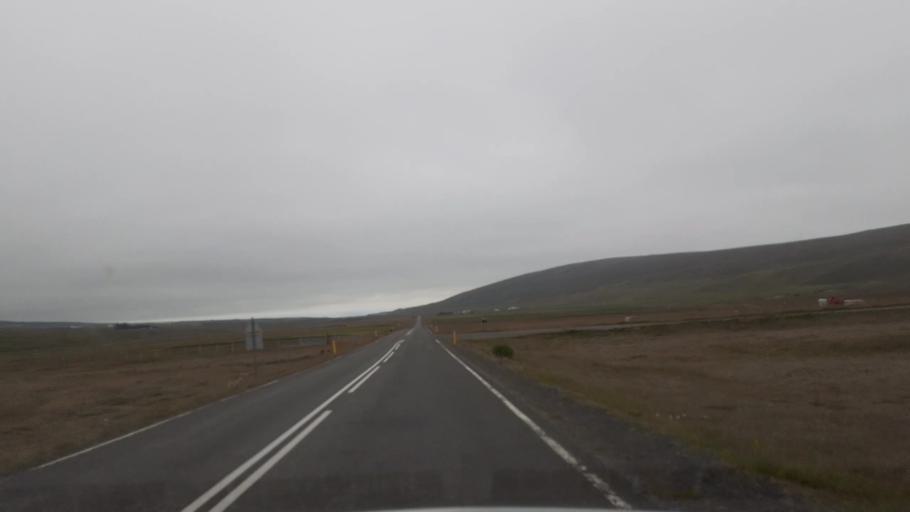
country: IS
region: Northeast
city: Siglufjoerdur
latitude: 65.7406
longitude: -19.1410
